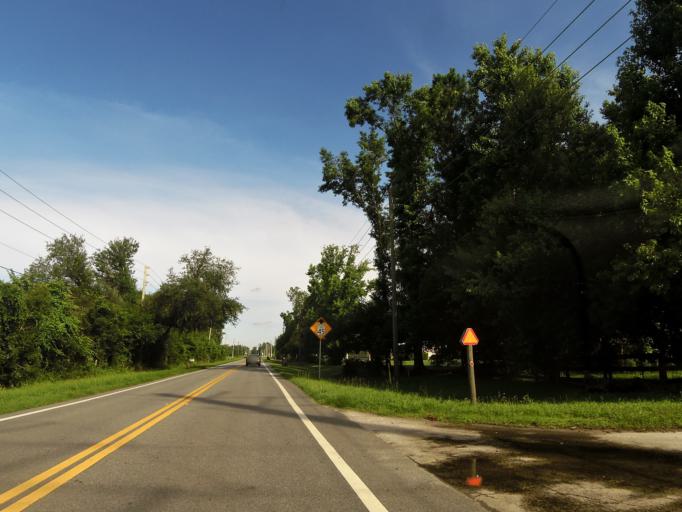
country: US
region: Florida
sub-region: Clay County
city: Green Cove Springs
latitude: 29.9864
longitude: -81.5272
